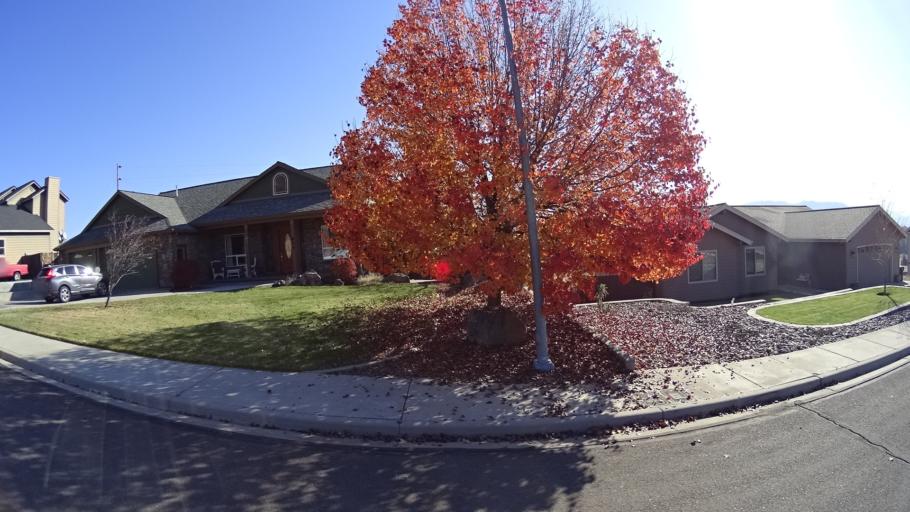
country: US
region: California
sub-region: Siskiyou County
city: Yreka
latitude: 41.7434
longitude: -122.6429
